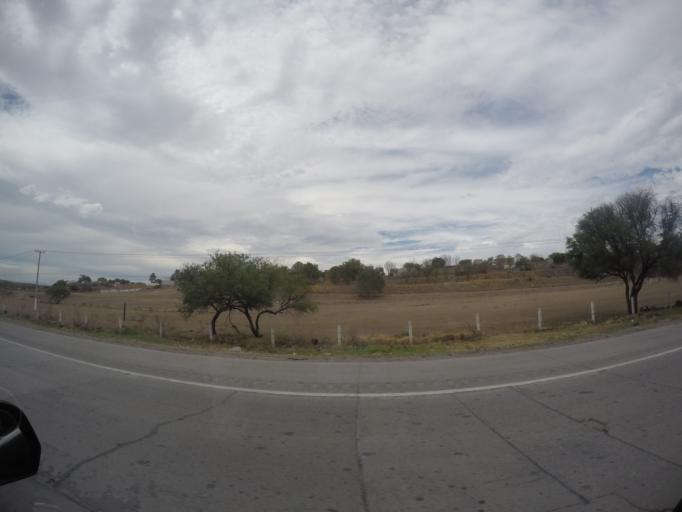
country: MX
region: Queretaro
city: San Juan del Rio
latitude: 20.3734
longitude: -99.9934
